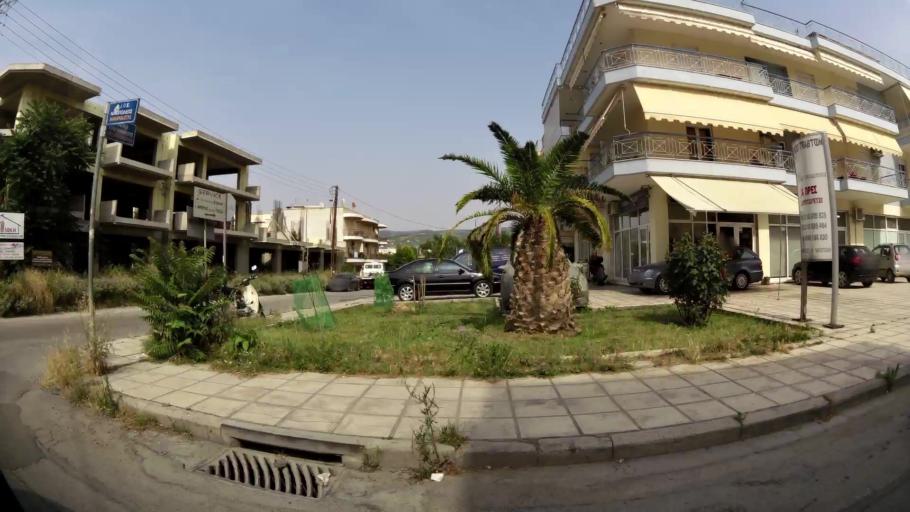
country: GR
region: Central Macedonia
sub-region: Nomos Thessalonikis
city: Stavroupoli
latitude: 40.6807
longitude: 22.9368
